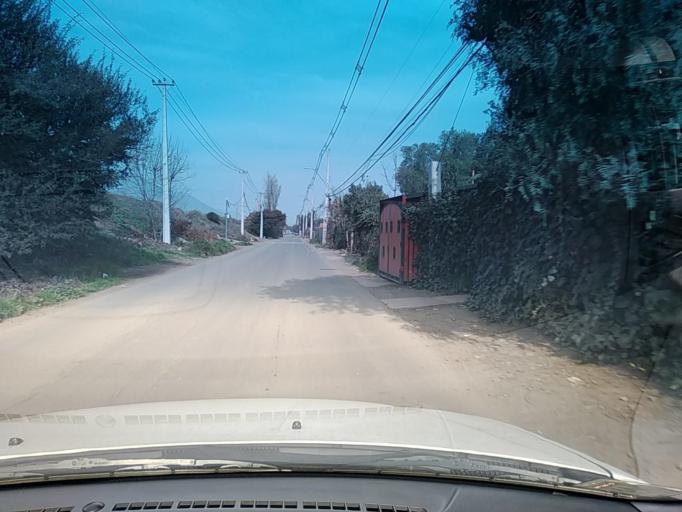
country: CL
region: Santiago Metropolitan
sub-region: Provincia de Chacabuco
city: Chicureo Abajo
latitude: -33.2978
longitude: -70.7224
